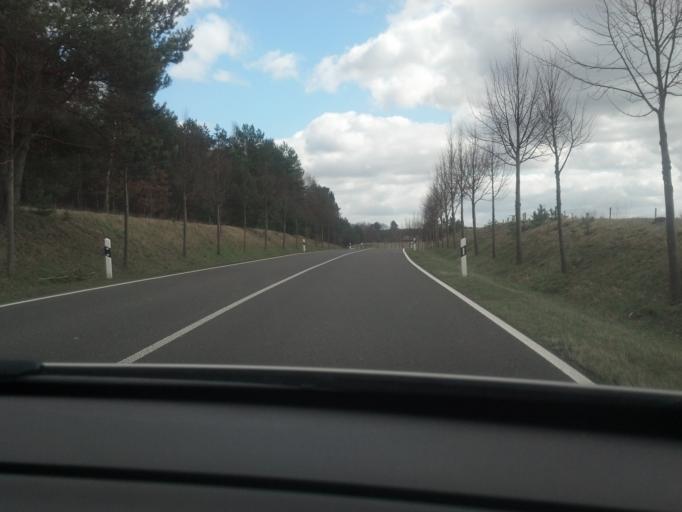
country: DE
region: Mecklenburg-Vorpommern
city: Neustrelitz
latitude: 53.3011
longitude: 13.0669
